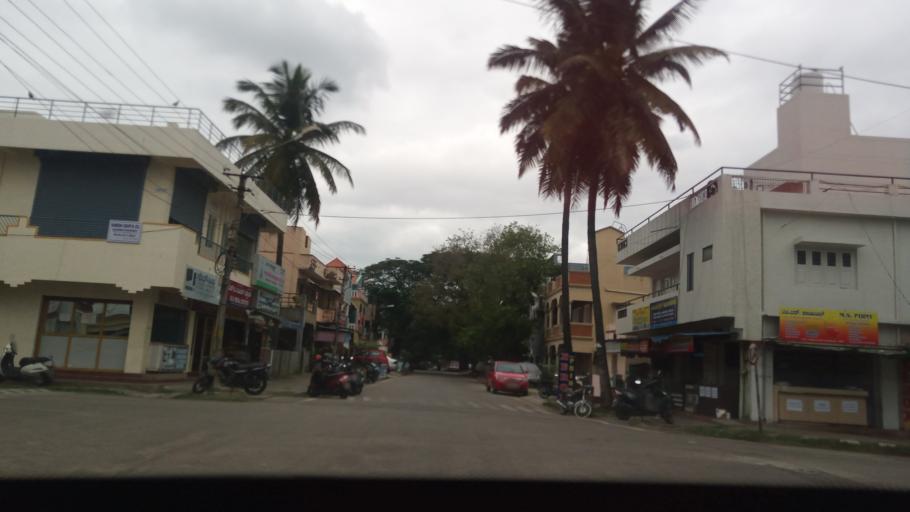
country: IN
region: Karnataka
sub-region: Mysore
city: Mysore
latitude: 12.3025
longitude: 76.6281
